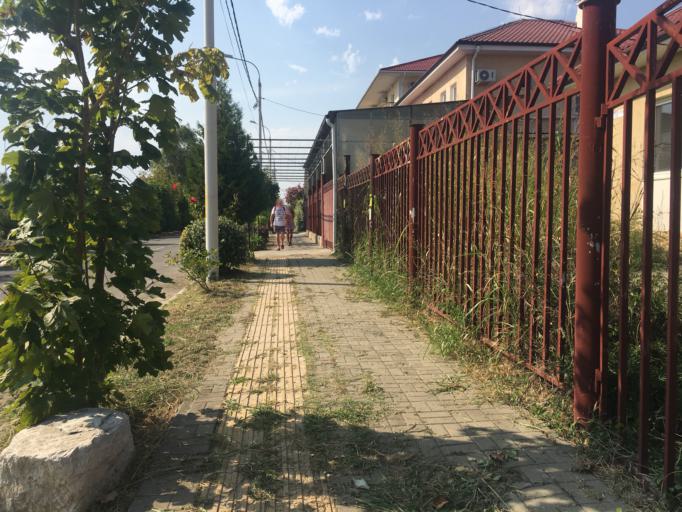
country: RU
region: Krasnodarskiy
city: Vysokoye
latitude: 43.3929
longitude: 40.0003
